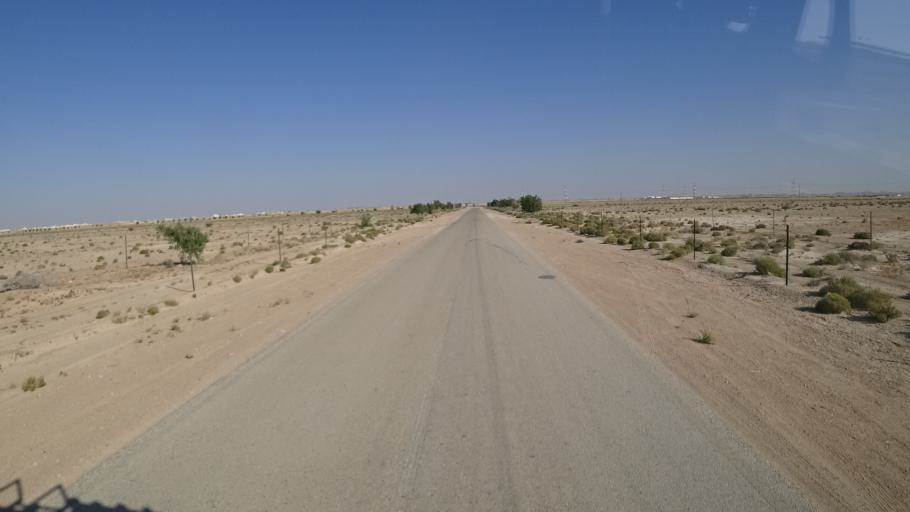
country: OM
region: Zufar
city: Salalah
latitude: 17.5957
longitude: 54.0277
